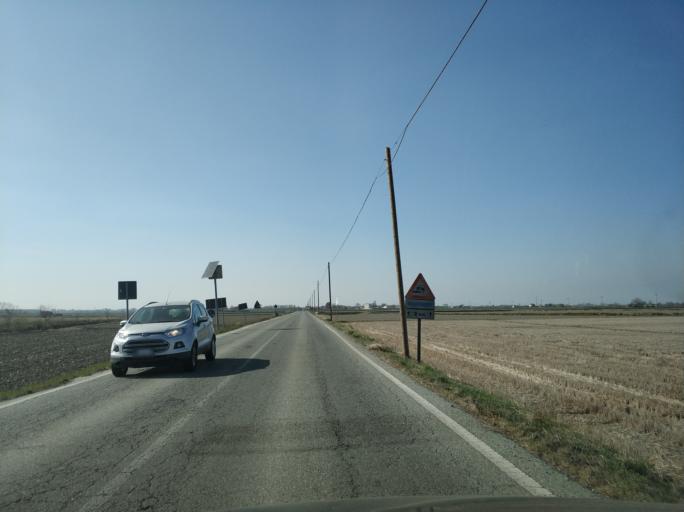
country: IT
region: Piedmont
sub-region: Provincia di Novara
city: Vinzaglio
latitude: 45.3158
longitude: 8.4945
